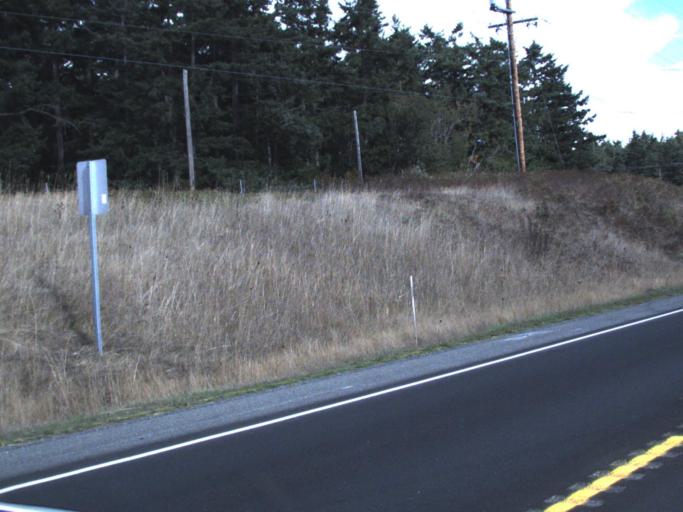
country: US
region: Washington
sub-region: Island County
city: Coupeville
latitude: 48.2123
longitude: -122.6946
